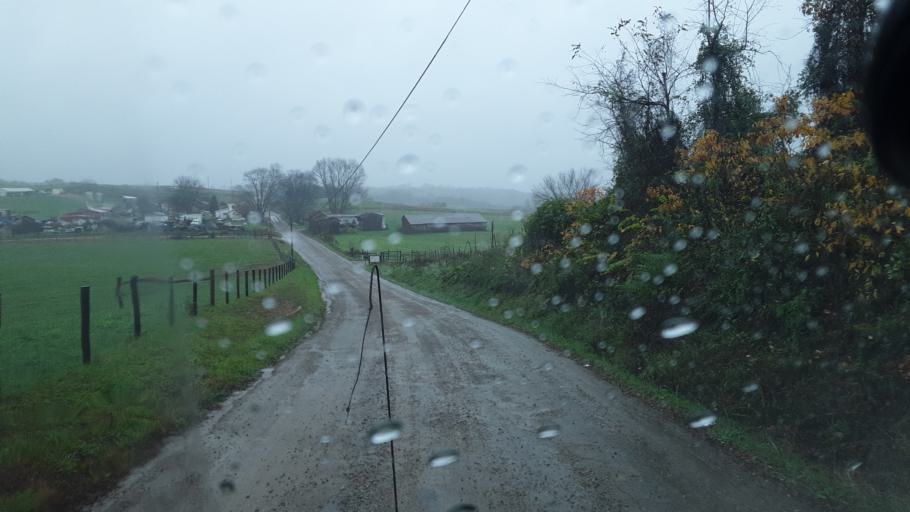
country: US
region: Ohio
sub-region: Vinton County
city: McArthur
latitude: 39.2259
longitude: -82.4746
